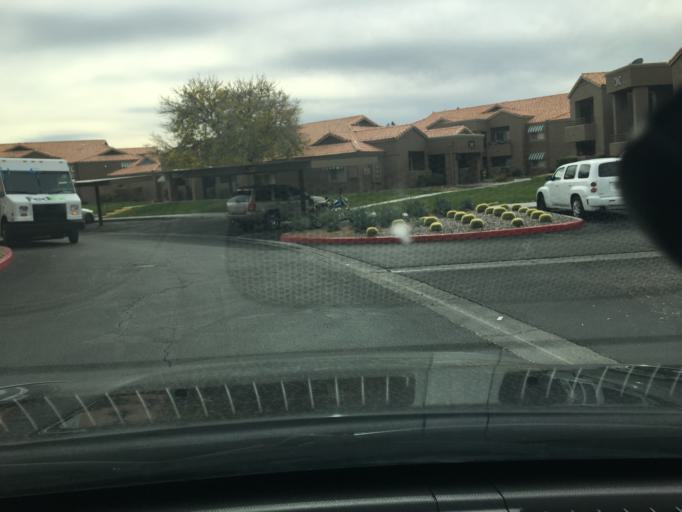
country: US
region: Nevada
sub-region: Clark County
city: Spring Valley
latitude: 36.1611
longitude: -115.2219
